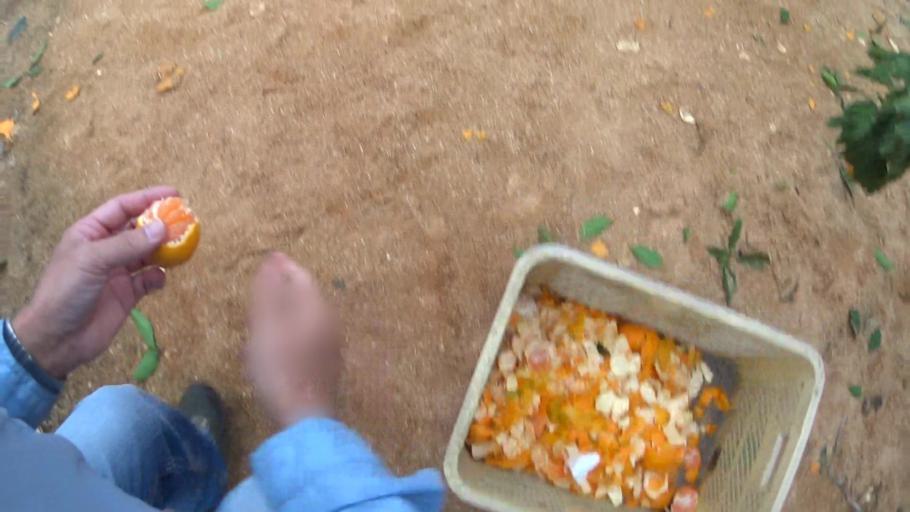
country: JP
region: Chiba
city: Nagareyama
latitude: 35.8404
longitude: 139.8827
